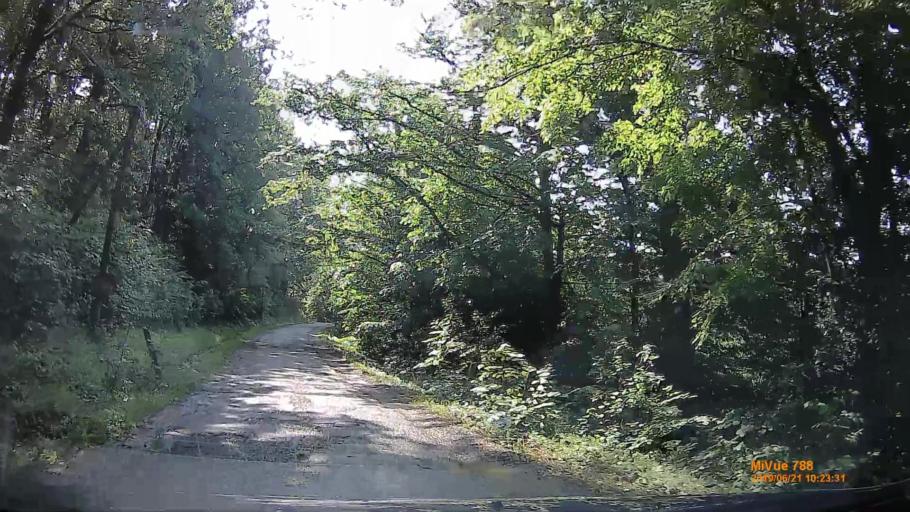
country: HU
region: Baranya
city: Buekkoesd
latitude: 46.1856
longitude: 17.9701
